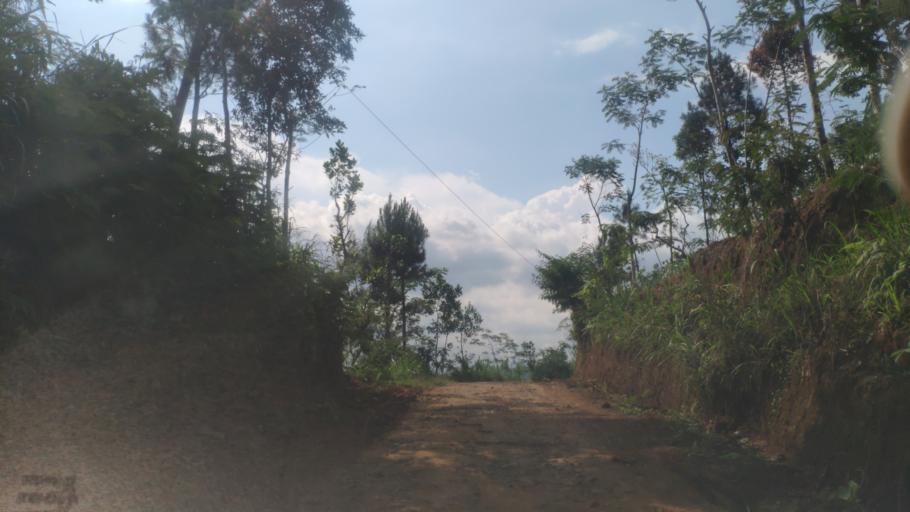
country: ID
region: Central Java
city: Buaran
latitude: -7.2457
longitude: 109.6856
